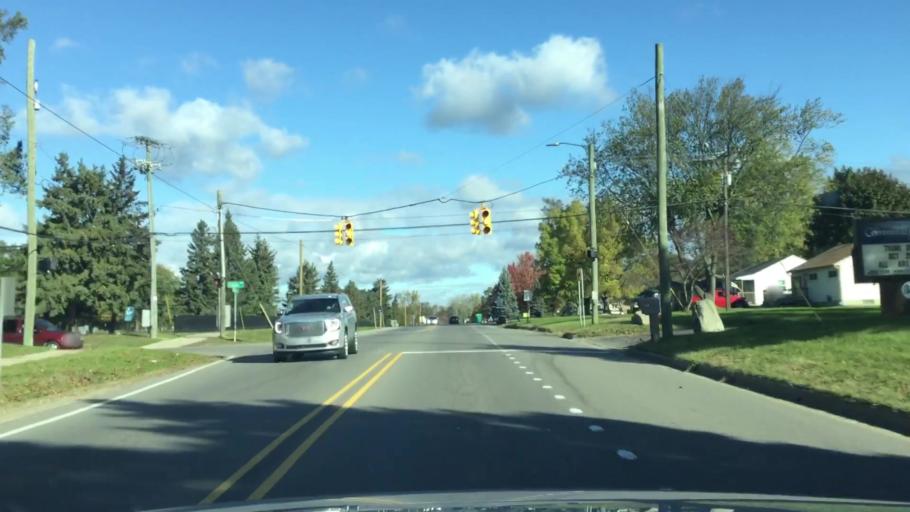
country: US
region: Michigan
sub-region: Oakland County
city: Waterford
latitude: 42.6674
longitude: -83.3866
